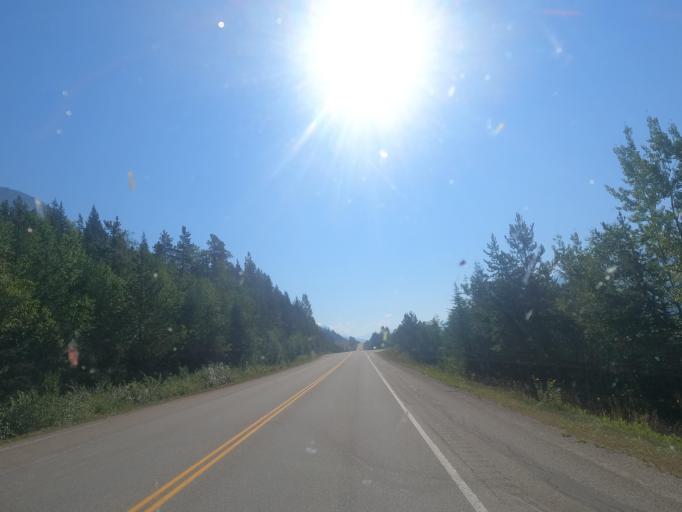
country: CA
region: Alberta
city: Jasper Park Lodge
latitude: 52.9713
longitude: -118.9375
